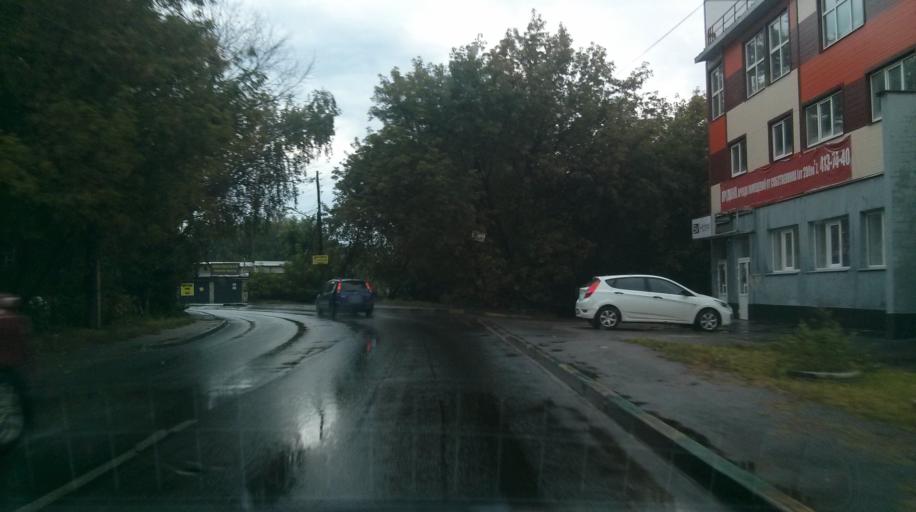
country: RU
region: Nizjnij Novgorod
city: Nizhniy Novgorod
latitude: 56.2570
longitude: 43.9860
